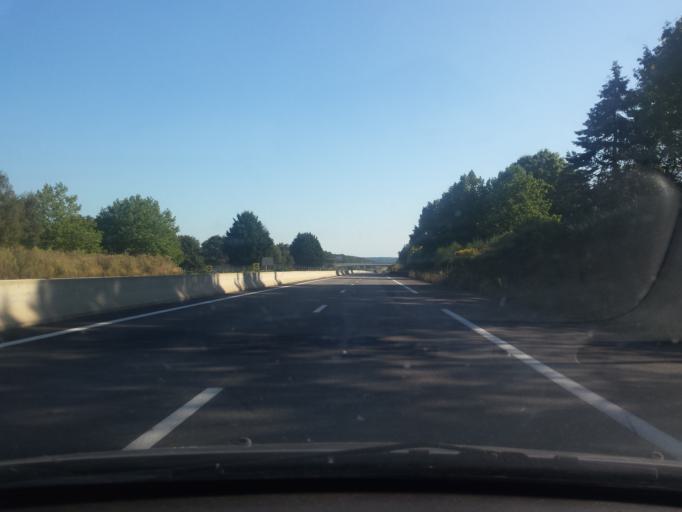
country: FR
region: Brittany
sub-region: Departement du Morbihan
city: Colpo
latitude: 47.8114
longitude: -2.8102
